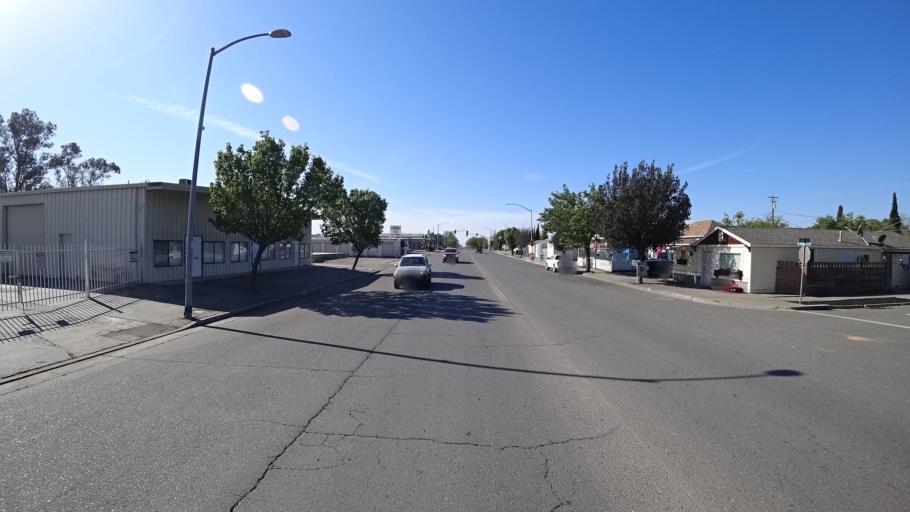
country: US
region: California
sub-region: Glenn County
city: Willows
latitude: 39.5255
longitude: -122.1940
